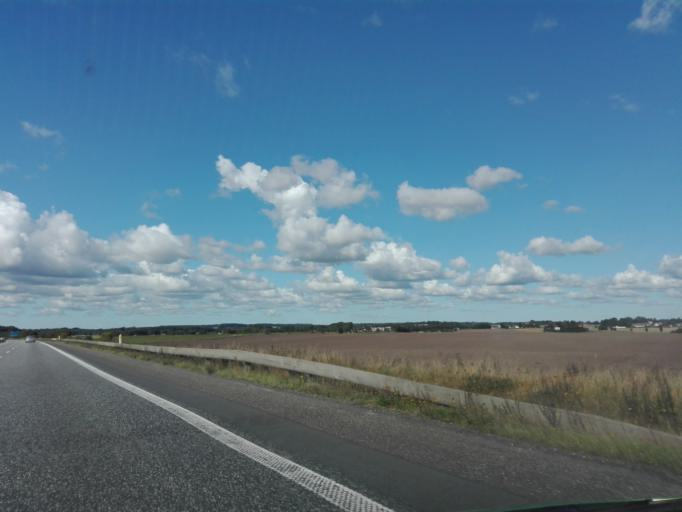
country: DK
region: Central Jutland
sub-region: Randers Kommune
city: Spentrup
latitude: 56.5329
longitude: 9.9276
